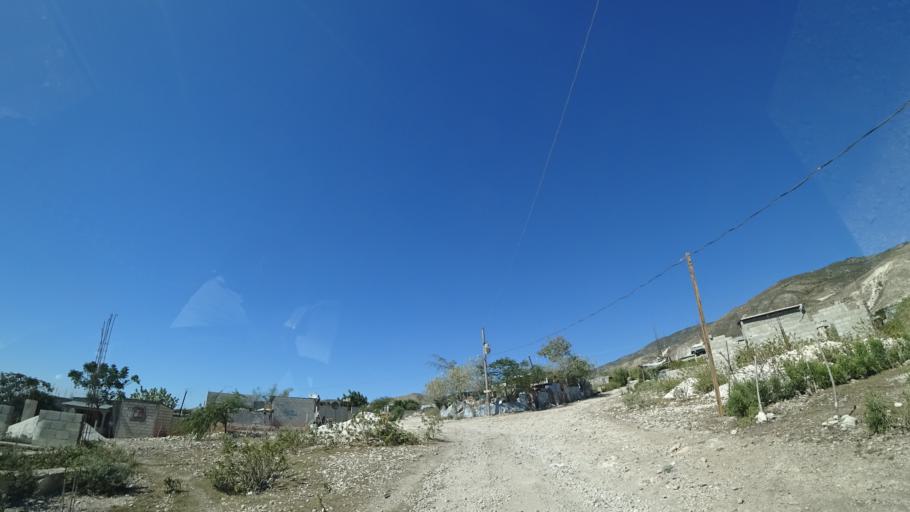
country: HT
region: Ouest
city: Croix des Bouquets
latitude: 18.6703
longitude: -72.2341
